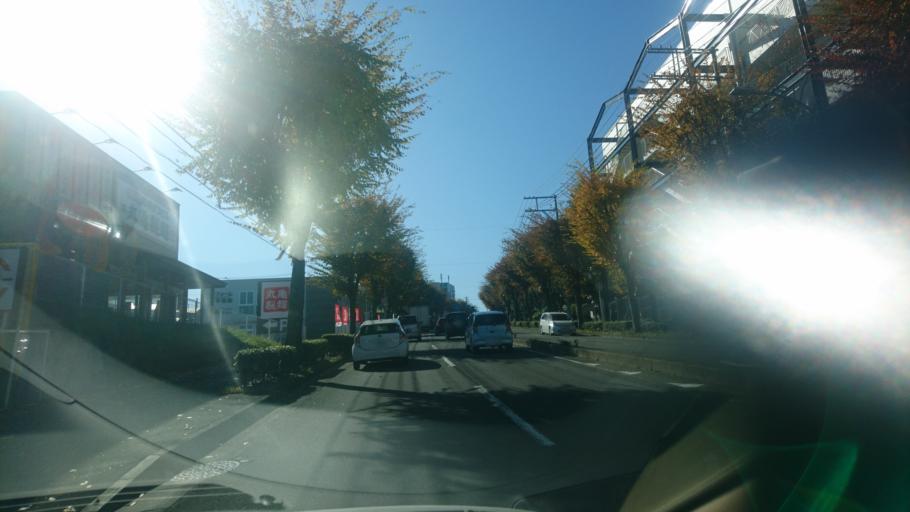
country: JP
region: Miyagi
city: Sendai-shi
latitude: 38.2993
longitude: 140.8295
